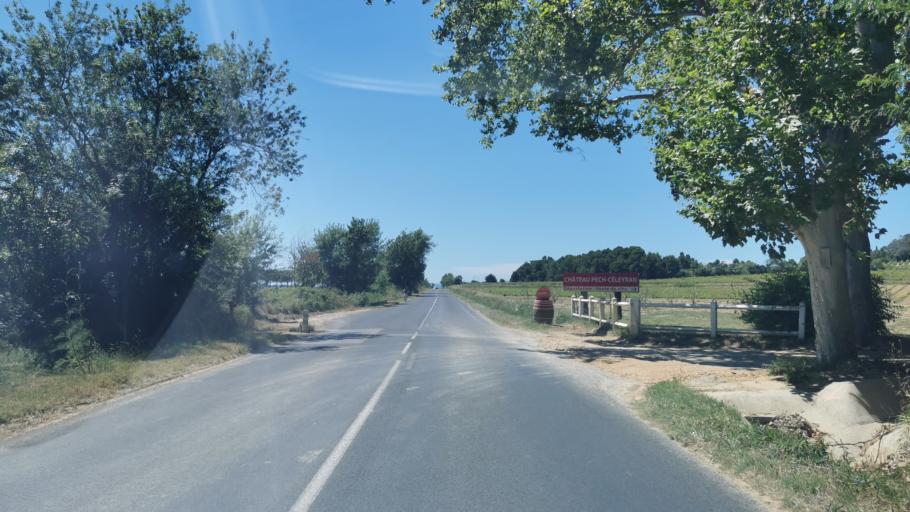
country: FR
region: Languedoc-Roussillon
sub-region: Departement de l'Aude
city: Vinassan
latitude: 43.2311
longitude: 3.0925
